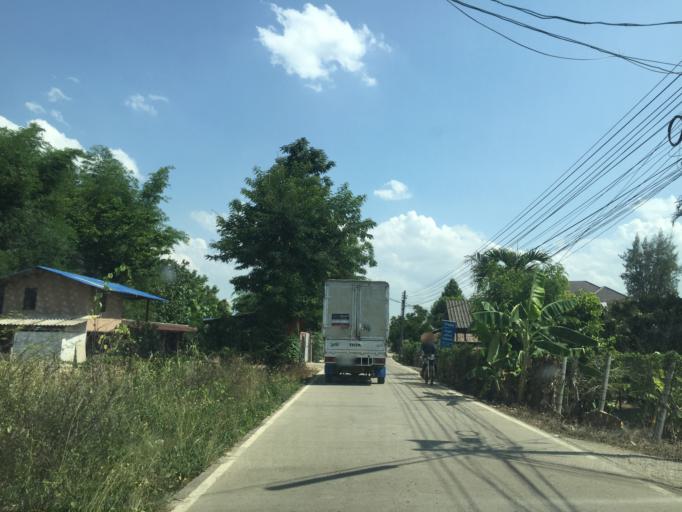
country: TH
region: Lamphun
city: Ban Thi
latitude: 18.6359
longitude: 99.0538
